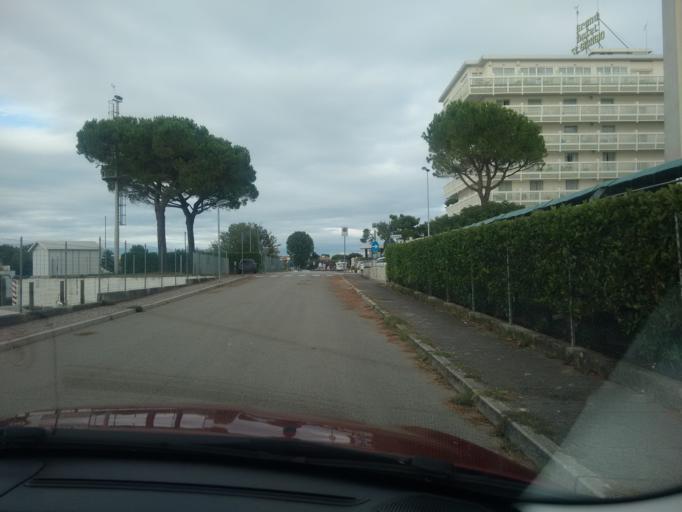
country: IT
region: Veneto
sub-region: Provincia di Venezia
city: Caorle
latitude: 45.5895
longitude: 12.8608
